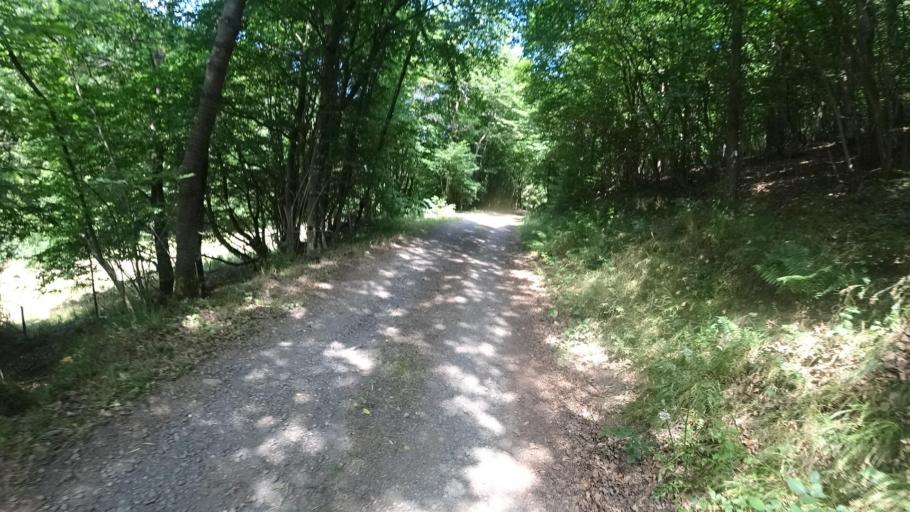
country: DE
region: Rheinland-Pfalz
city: Heckenbach
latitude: 50.4875
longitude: 7.0867
